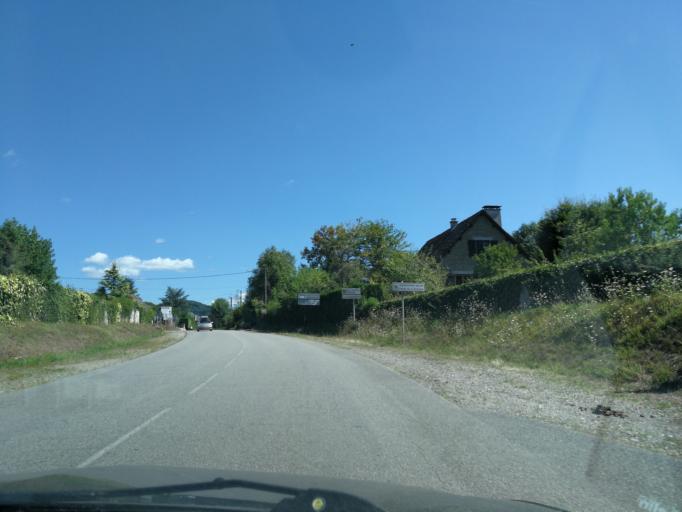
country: FR
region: Limousin
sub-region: Departement de la Correze
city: Argentat
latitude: 45.0894
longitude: 1.9286
